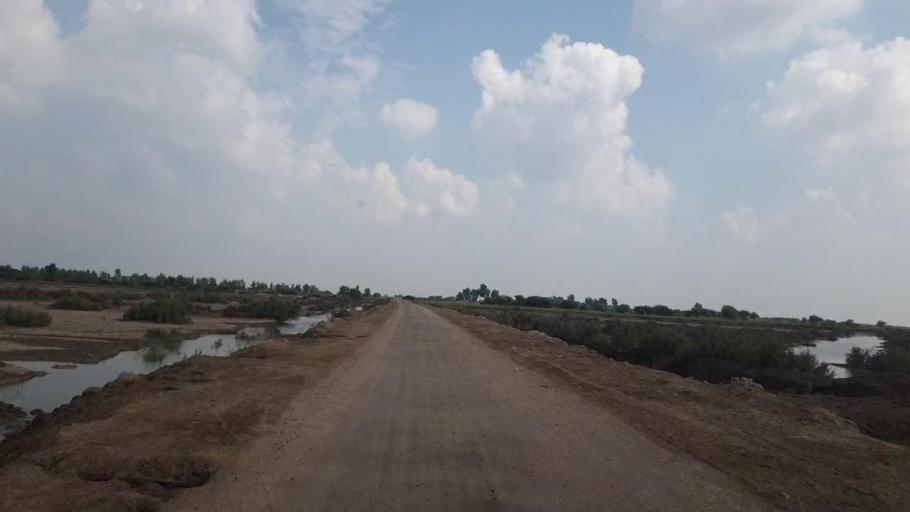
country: PK
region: Sindh
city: Badin
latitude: 24.5328
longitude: 68.6096
